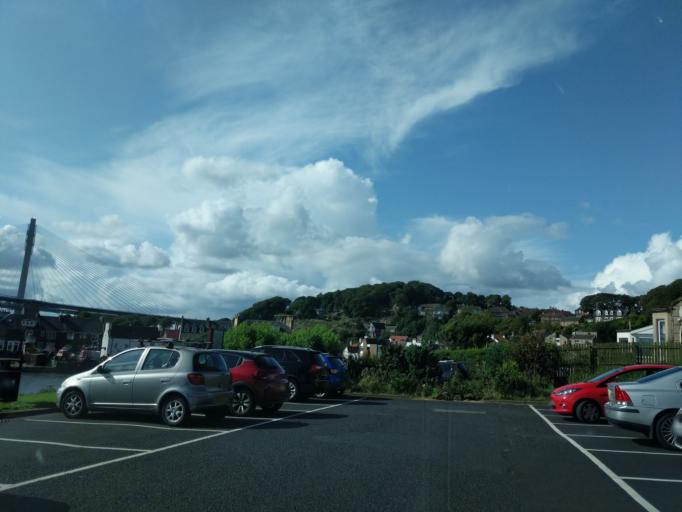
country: GB
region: Scotland
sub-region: Fife
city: North Queensferry
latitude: 56.0079
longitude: -3.3925
